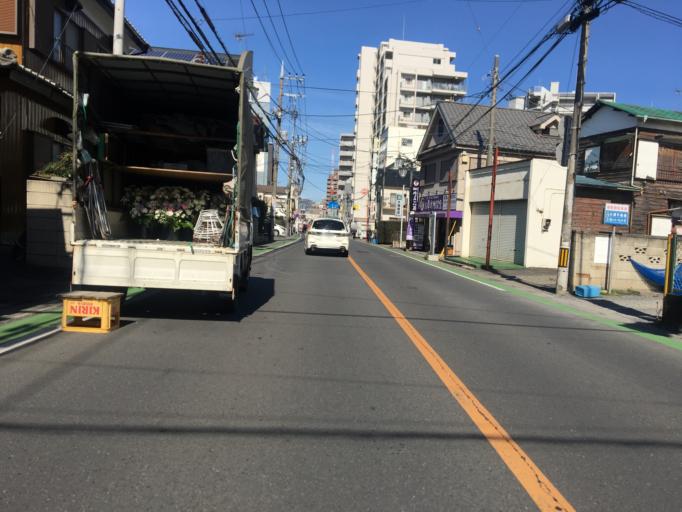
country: JP
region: Saitama
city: Shiki
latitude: 35.8214
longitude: 139.5722
